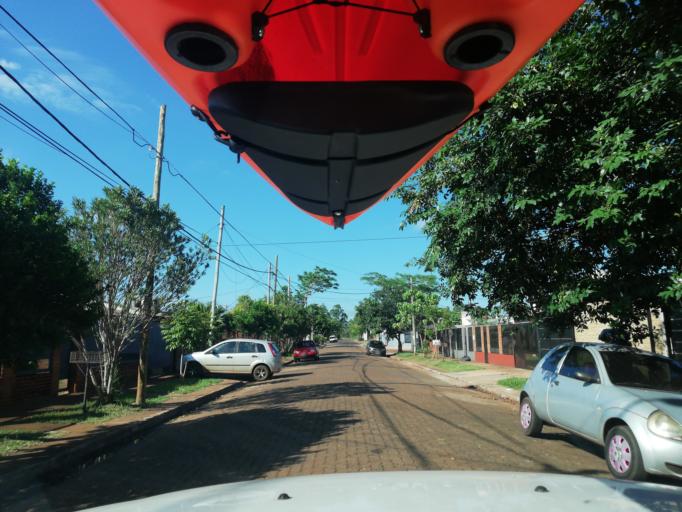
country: AR
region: Misiones
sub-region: Departamento de Capital
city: Posadas
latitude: -27.4244
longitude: -55.9387
